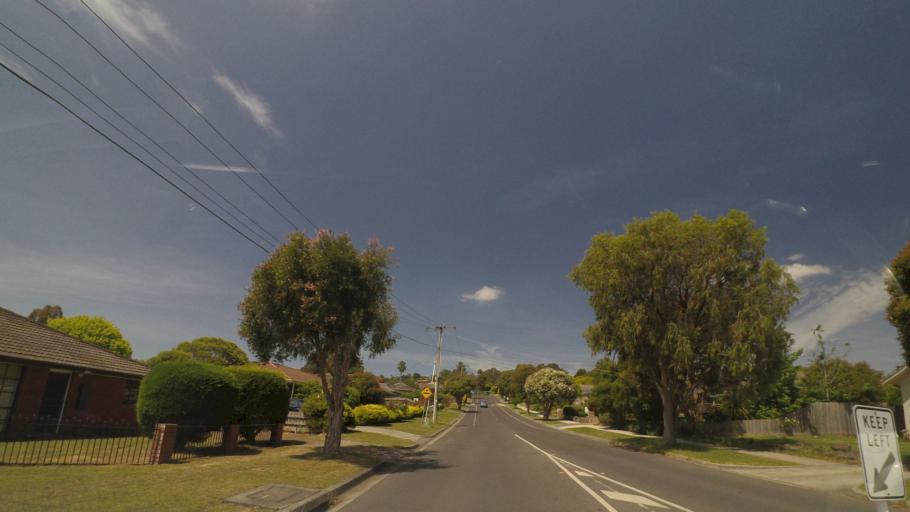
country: AU
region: Victoria
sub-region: Yarra Ranges
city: Chirnside Park
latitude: -37.7547
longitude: 145.3113
